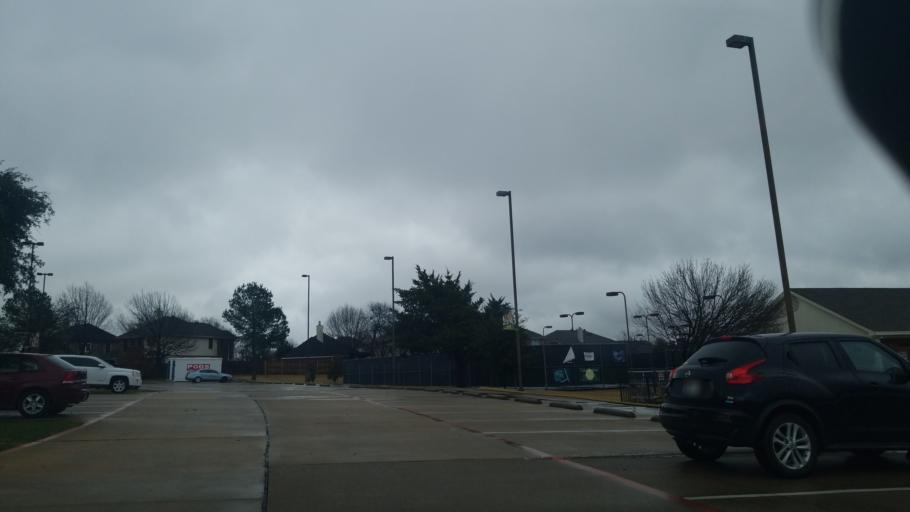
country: US
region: Texas
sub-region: Denton County
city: Corinth
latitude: 33.1511
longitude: -97.0880
